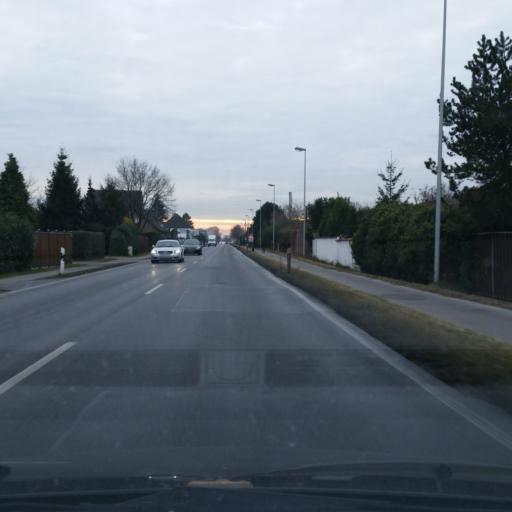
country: DE
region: North Rhine-Westphalia
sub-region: Regierungsbezirk Dusseldorf
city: Bocholt
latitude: 51.8141
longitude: 6.6119
